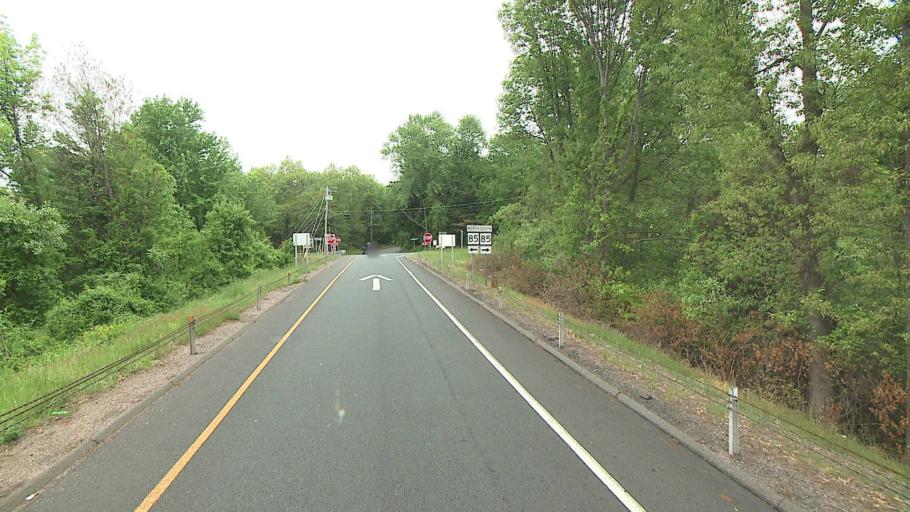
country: US
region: Connecticut
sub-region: Hartford County
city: Manchester
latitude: 41.7774
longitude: -72.4619
